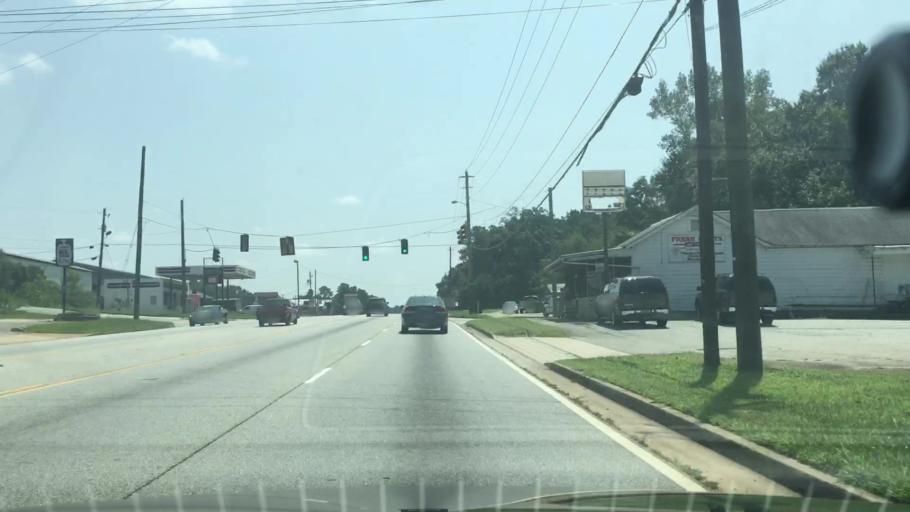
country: US
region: Georgia
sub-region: Spalding County
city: East Griffin
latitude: 33.2393
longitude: -84.2463
